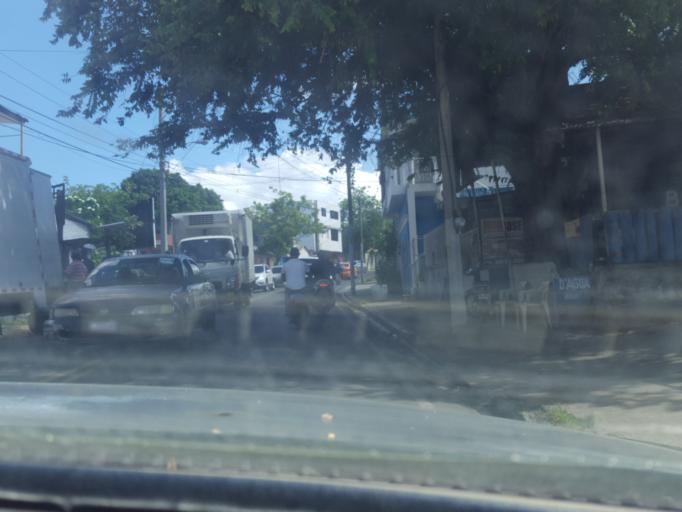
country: DO
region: Santiago
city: Santiago de los Caballeros
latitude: 19.4749
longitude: -70.7104
